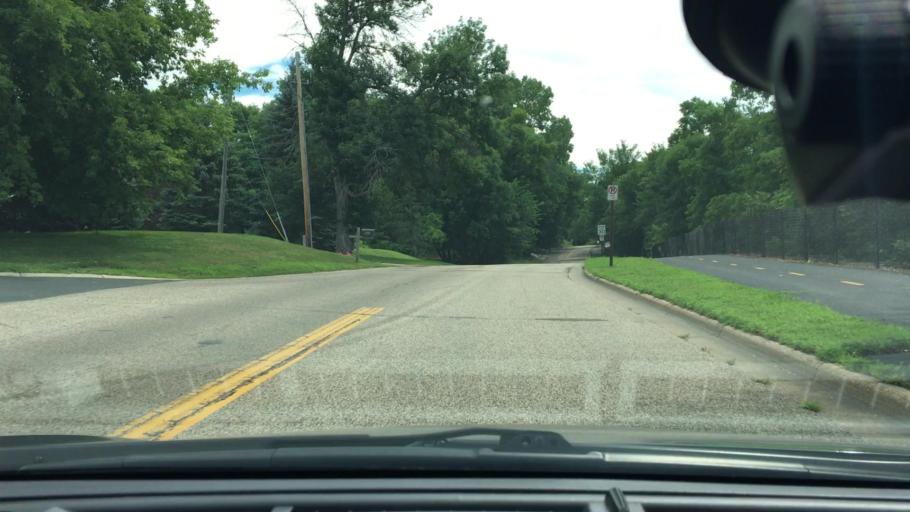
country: US
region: Minnesota
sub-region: Hennepin County
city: Plymouth
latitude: 45.0149
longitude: -93.4173
